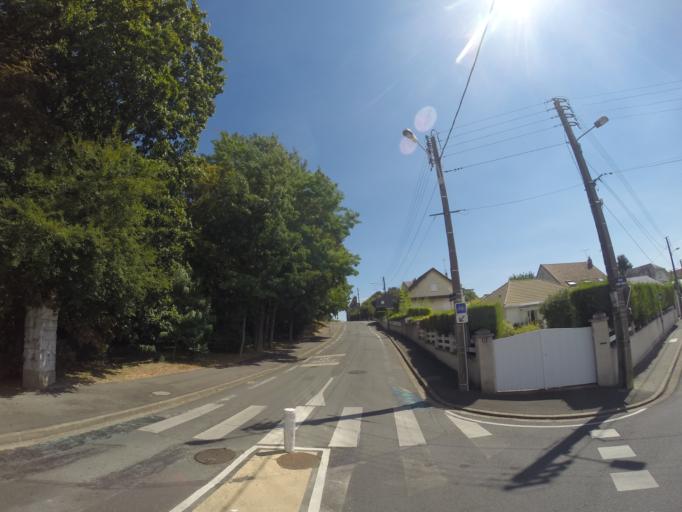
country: FR
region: Centre
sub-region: Departement d'Indre-et-Loire
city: Tours
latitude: 47.4094
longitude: 0.7077
